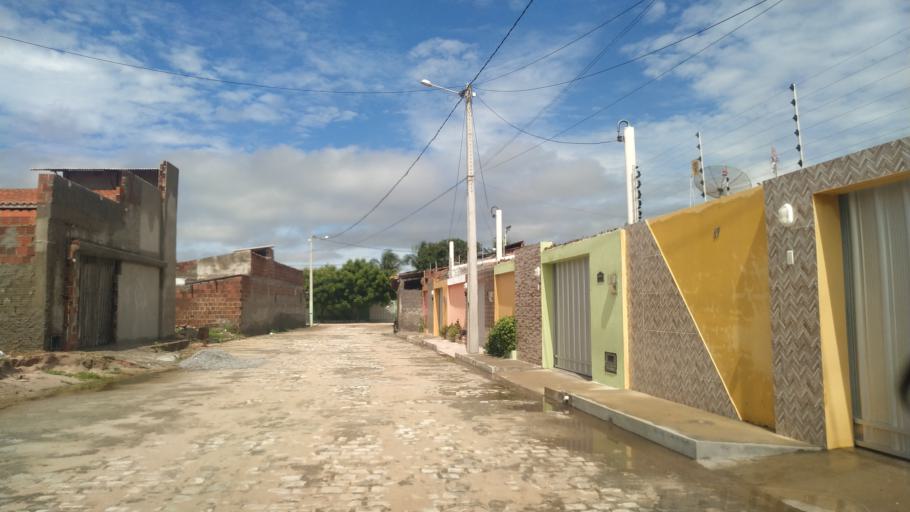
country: BR
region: Rio Grande do Norte
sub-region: Areia Branca
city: Areia Branca
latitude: -4.9526
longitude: -37.1235
